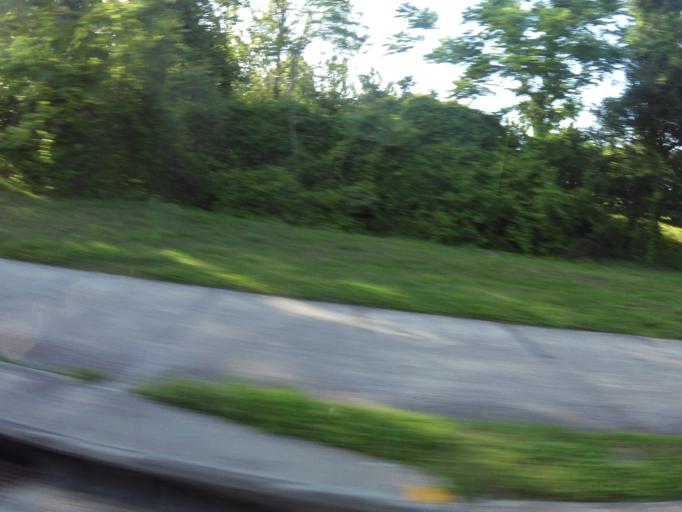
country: US
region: Florida
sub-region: Saint Johns County
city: Villano Beach
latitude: 29.9728
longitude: -81.4791
